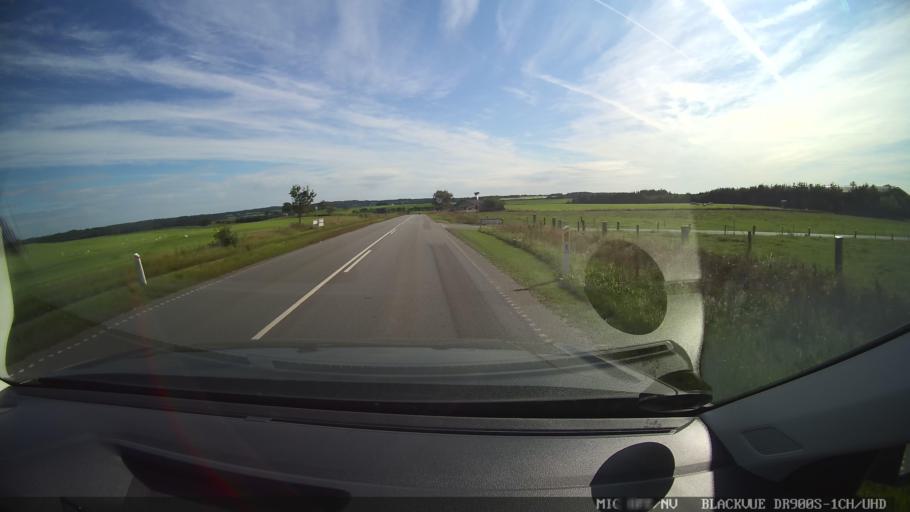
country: DK
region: North Denmark
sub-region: Mariagerfjord Kommune
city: Arden
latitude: 56.7642
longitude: 9.8826
